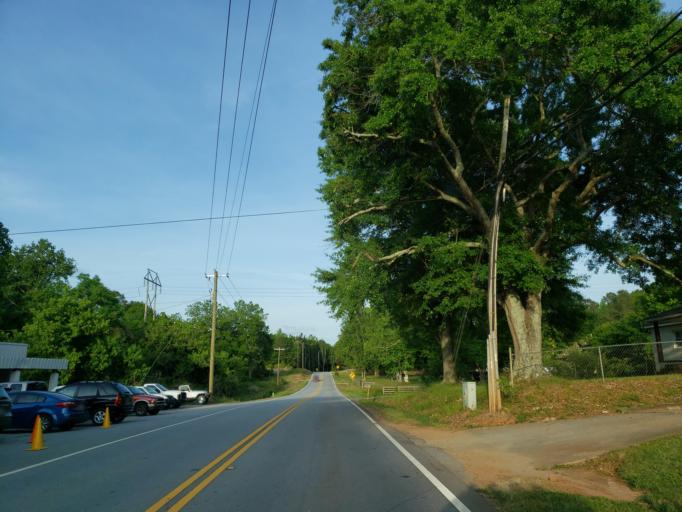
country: US
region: Georgia
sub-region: Carroll County
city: Carrollton
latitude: 33.5920
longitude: -85.1271
